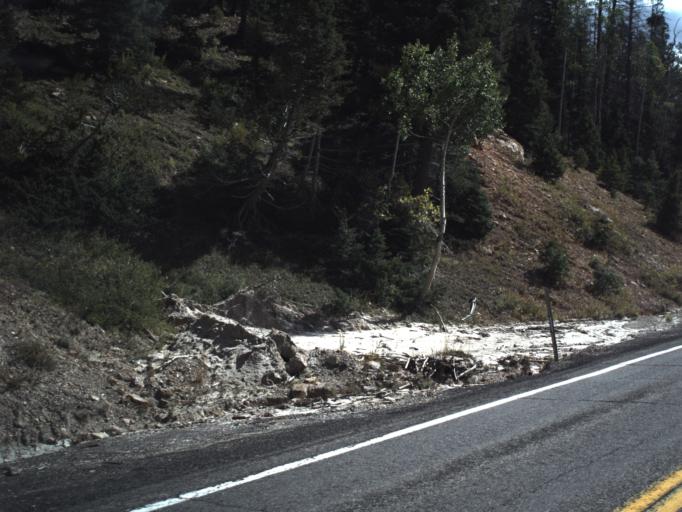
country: US
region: Utah
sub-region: Iron County
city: Cedar City
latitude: 37.5861
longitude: -112.8836
